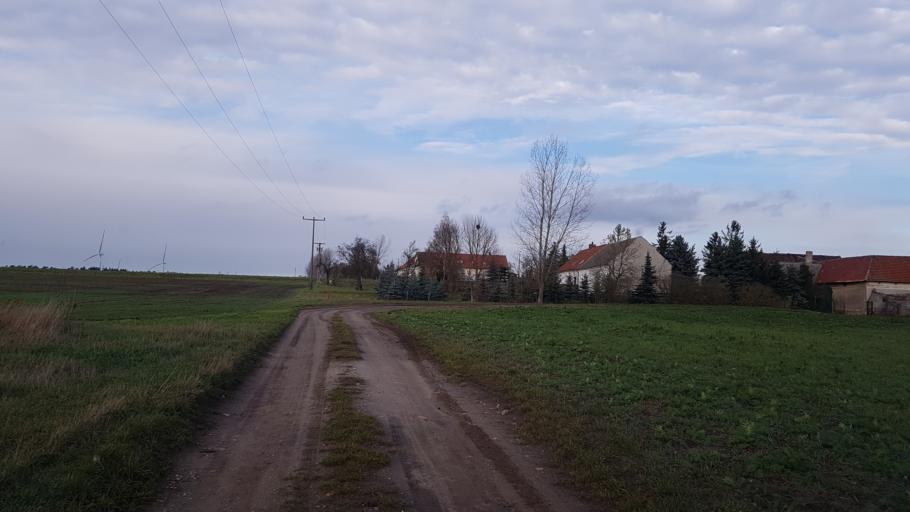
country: DE
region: Brandenburg
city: Trobitz
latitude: 51.6525
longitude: 13.4114
